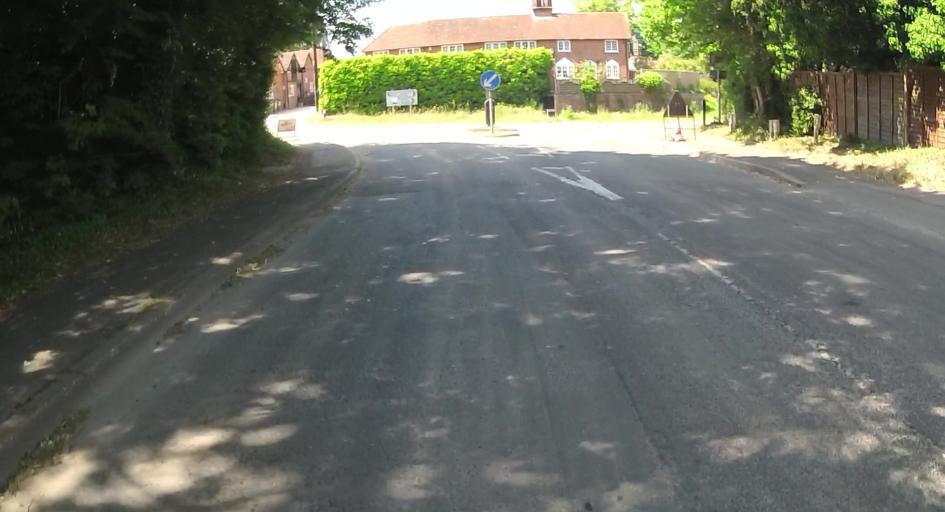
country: GB
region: England
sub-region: Hampshire
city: Basingstoke
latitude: 51.2969
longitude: -1.1134
